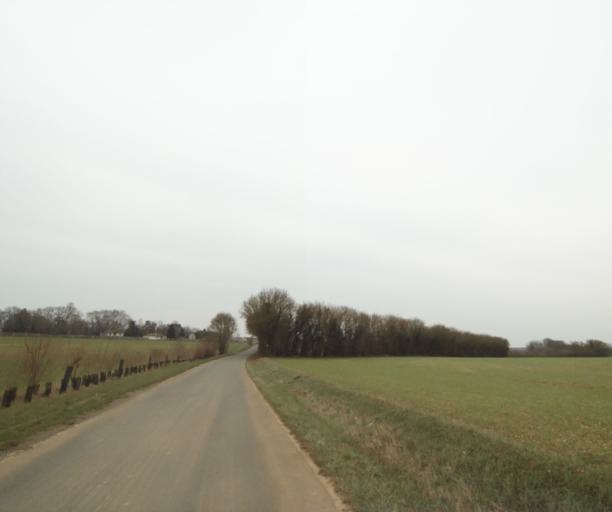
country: FR
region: Poitou-Charentes
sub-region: Departement des Deux-Sevres
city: Magne
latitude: 46.3345
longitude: -0.5203
